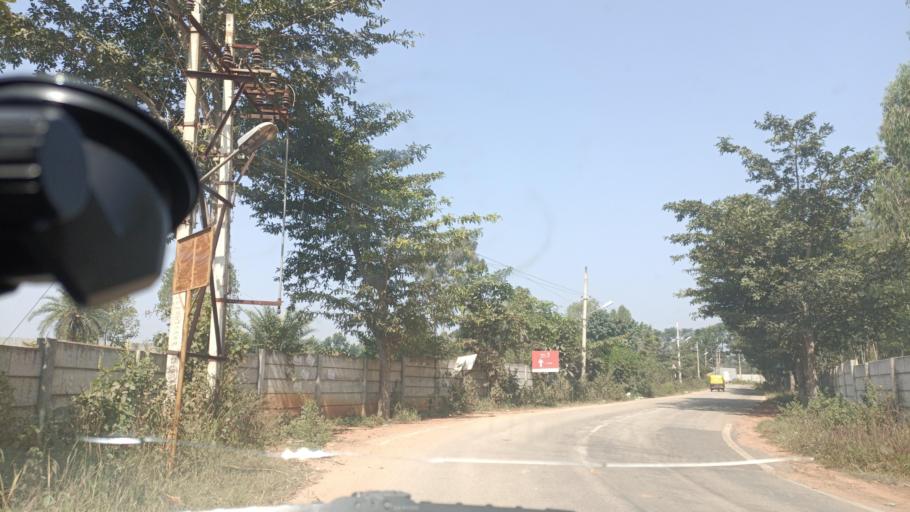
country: IN
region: Karnataka
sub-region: Bangalore Urban
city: Yelahanka
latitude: 13.1236
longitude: 77.6007
